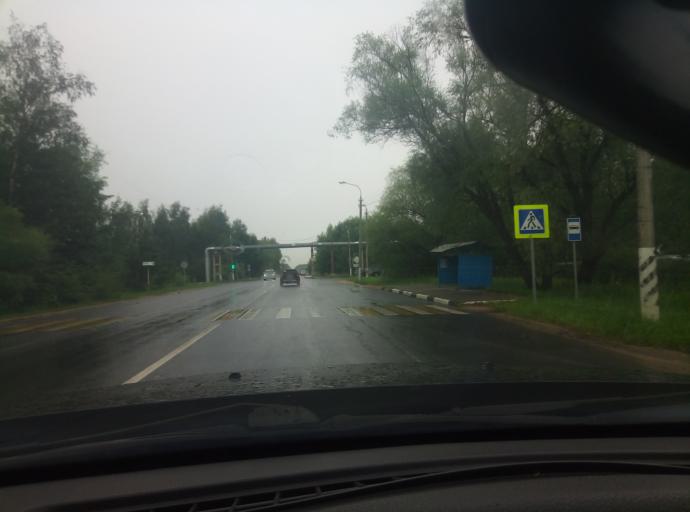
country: RU
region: Moskovskaya
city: Protvino
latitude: 54.8831
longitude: 37.2129
